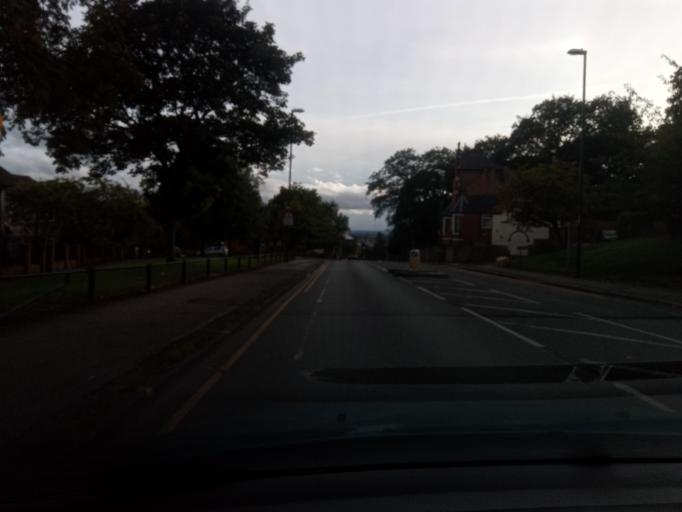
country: GB
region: England
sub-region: Nottingham
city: Nottingham
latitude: 52.9667
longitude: -1.1438
